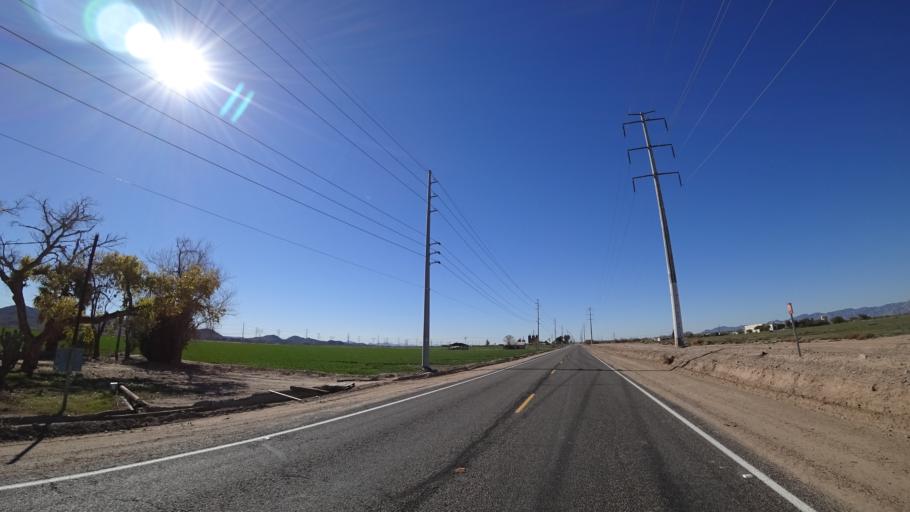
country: US
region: Arizona
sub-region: Maricopa County
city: Goodyear
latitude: 33.4065
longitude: -112.3708
